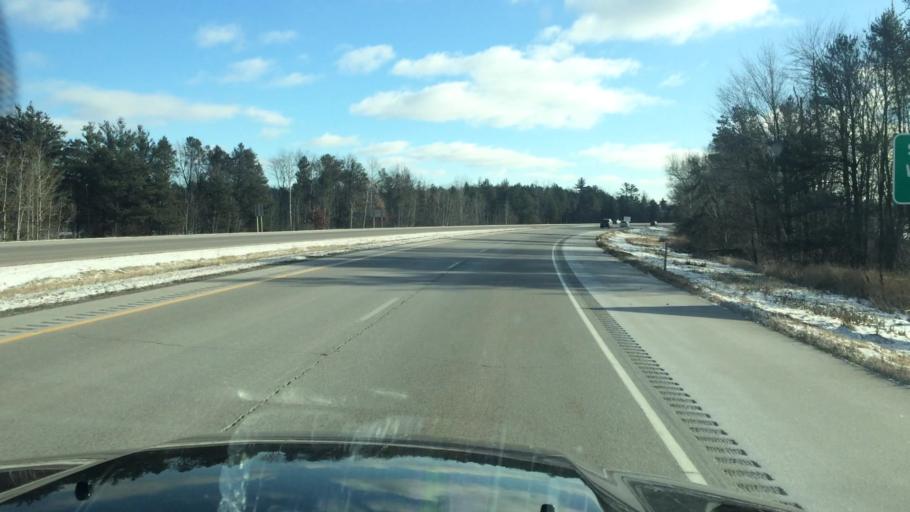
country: US
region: Wisconsin
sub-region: Portage County
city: Stevens Point
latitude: 44.5479
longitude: -89.5547
